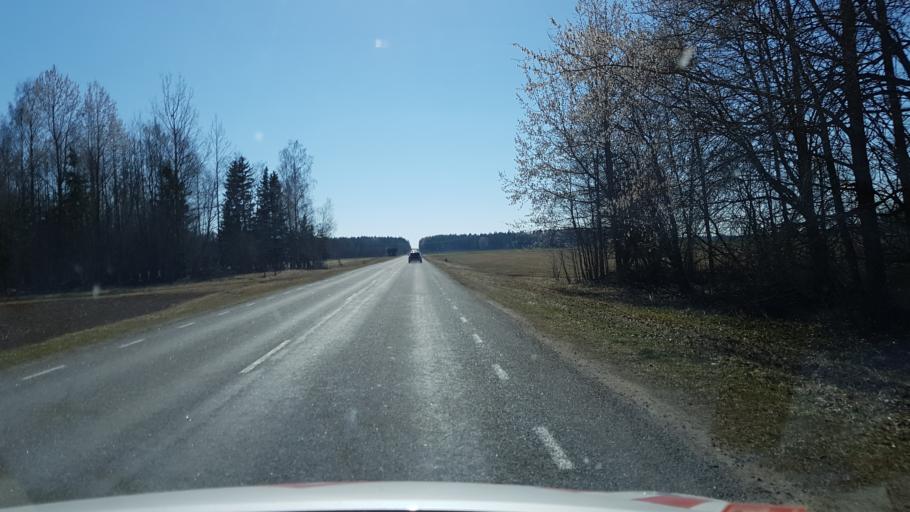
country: EE
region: Laeaene-Virumaa
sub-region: Tamsalu vald
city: Tamsalu
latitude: 59.1382
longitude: 26.0497
